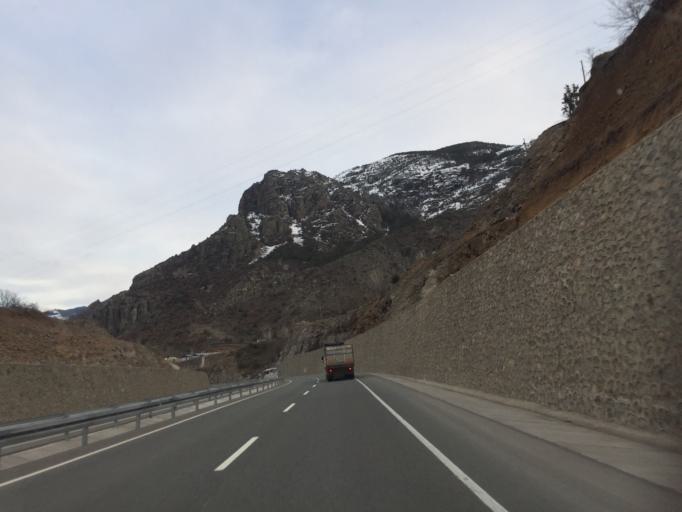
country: TR
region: Gumushane
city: Gumushkhane
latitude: 40.5020
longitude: 39.4291
